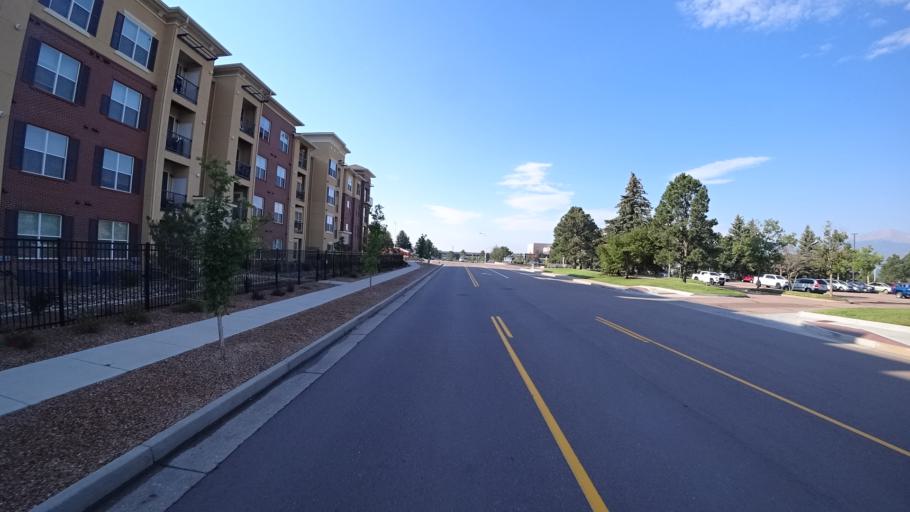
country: US
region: Colorado
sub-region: El Paso County
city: Air Force Academy
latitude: 38.9595
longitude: -104.7963
